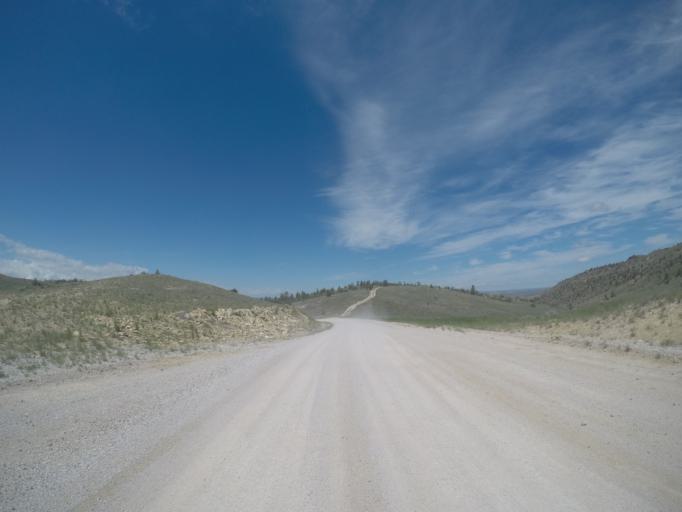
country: US
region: Montana
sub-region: Carbon County
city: Red Lodge
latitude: 45.2070
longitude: -108.7939
